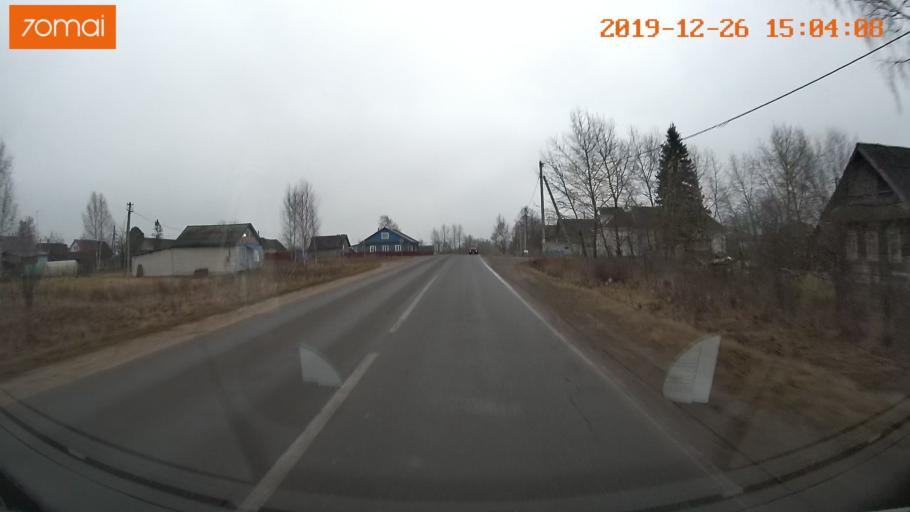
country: RU
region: Jaroslavl
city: Rybinsk
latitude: 58.2034
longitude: 38.8650
